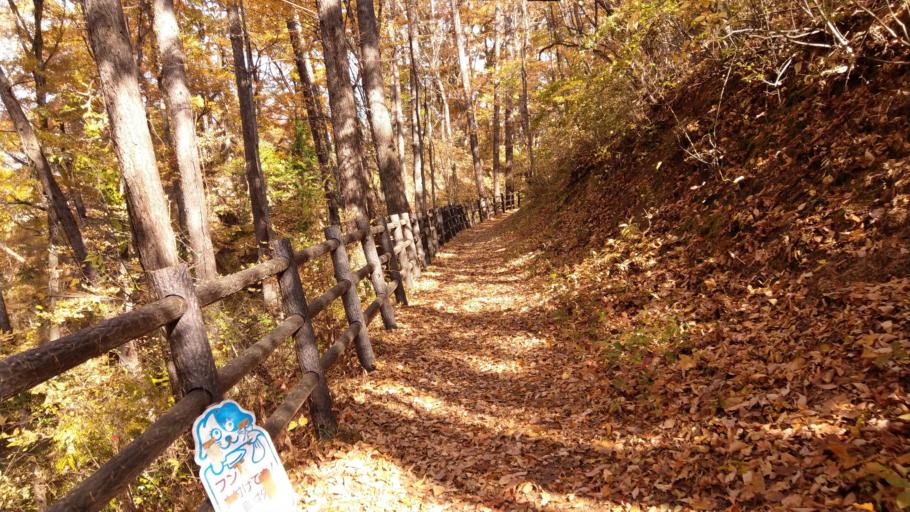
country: JP
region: Nagano
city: Komoro
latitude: 36.3176
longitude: 138.4255
